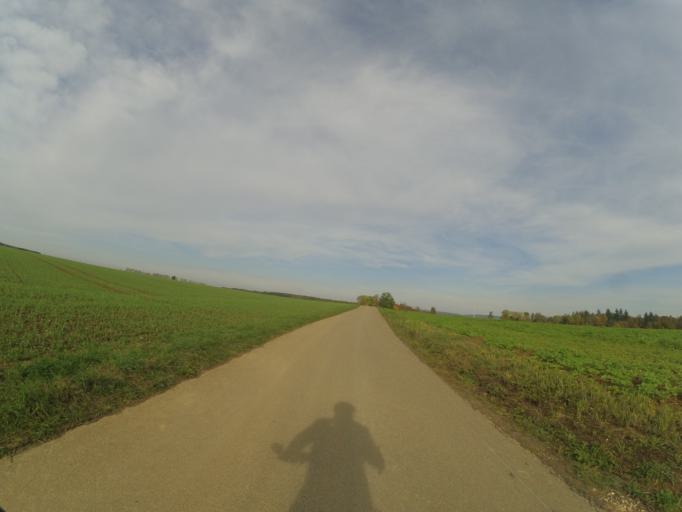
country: DE
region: Baden-Wuerttemberg
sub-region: Tuebingen Region
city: Blaubeuren
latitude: 48.4373
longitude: 9.8643
